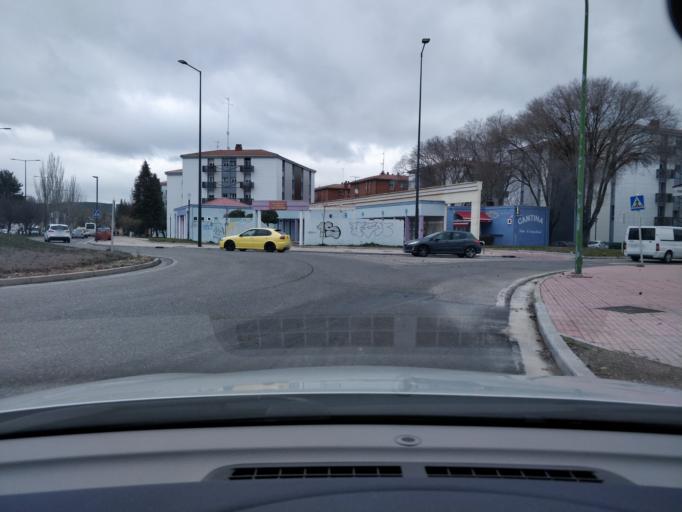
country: ES
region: Castille and Leon
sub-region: Provincia de Burgos
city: Burgos
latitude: 42.3621
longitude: -3.6530
